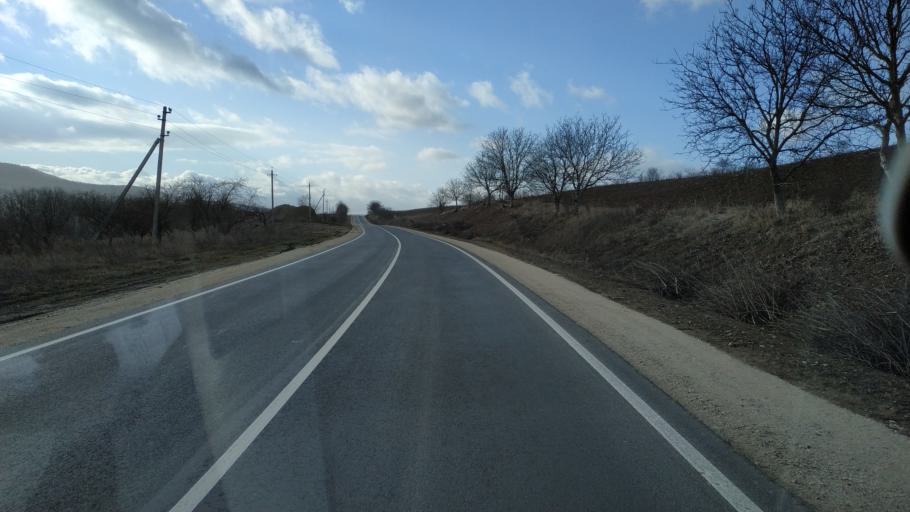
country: MD
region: Calarasi
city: Calarasi
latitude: 47.2944
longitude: 28.1691
